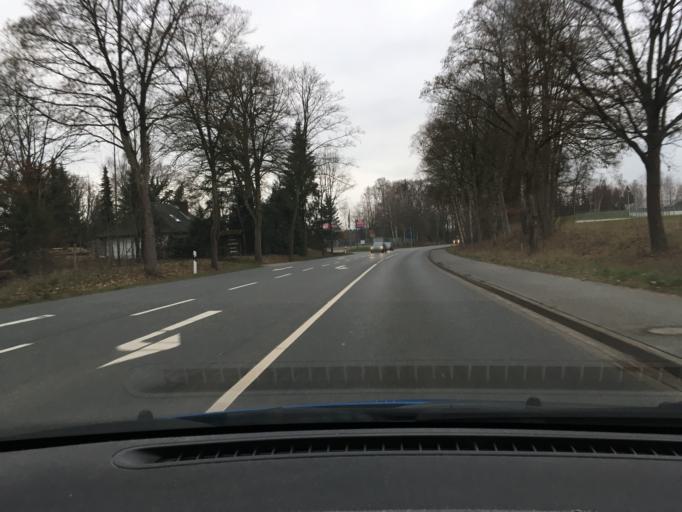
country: DE
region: Lower Saxony
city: Bomlitz
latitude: 52.8649
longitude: 9.6342
